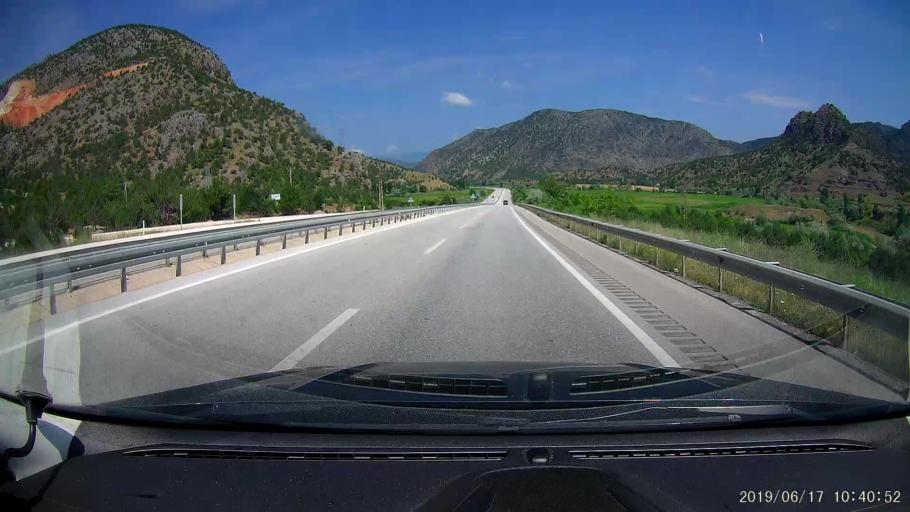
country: TR
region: Corum
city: Kargi
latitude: 41.0309
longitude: 34.5877
